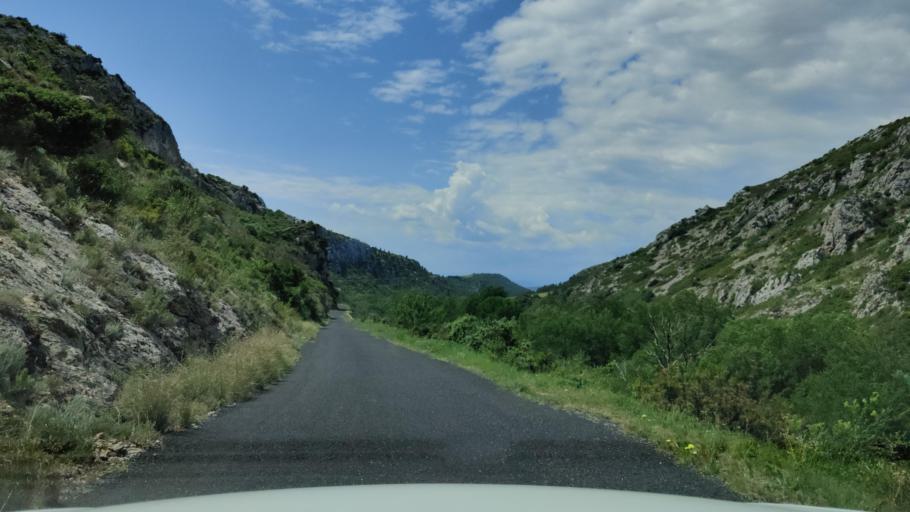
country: FR
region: Languedoc-Roussillon
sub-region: Departement des Pyrenees-Orientales
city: Estagel
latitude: 42.8067
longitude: 2.7392
